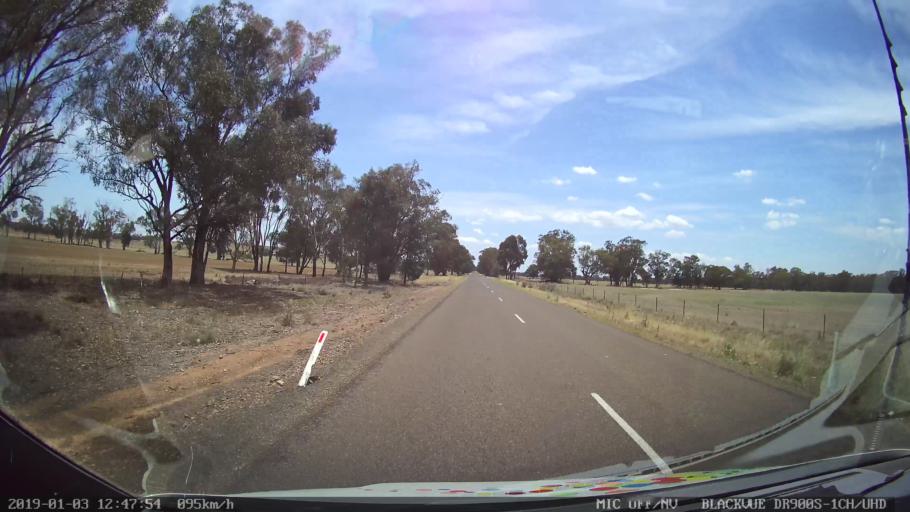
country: AU
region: New South Wales
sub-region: Weddin
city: Grenfell
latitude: -33.7211
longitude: 148.2459
